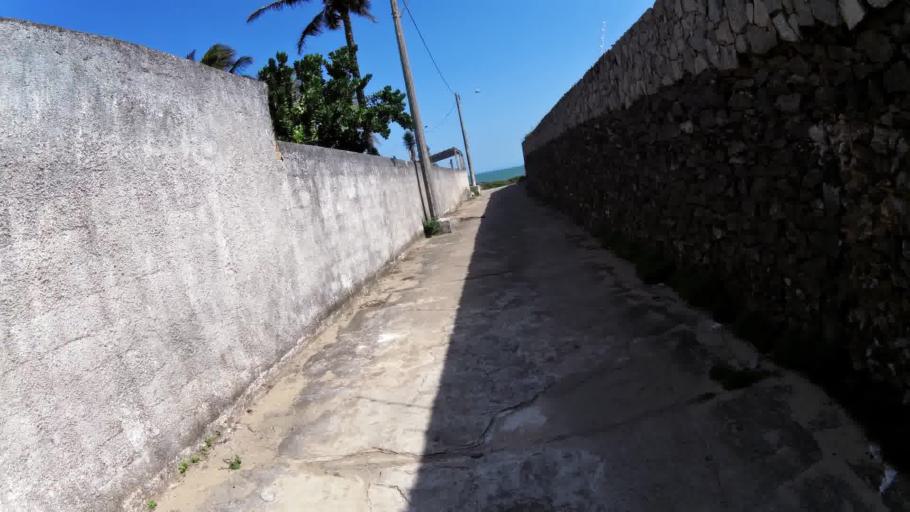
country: BR
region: Espirito Santo
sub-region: Guarapari
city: Guarapari
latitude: -20.7296
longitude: -40.5226
